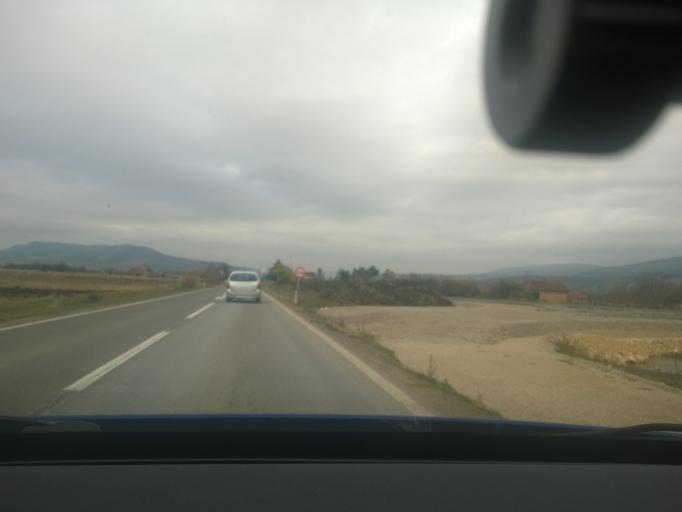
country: RS
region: Central Serbia
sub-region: Pirotski Okrug
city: Pirot
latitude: 43.1244
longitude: 22.6178
